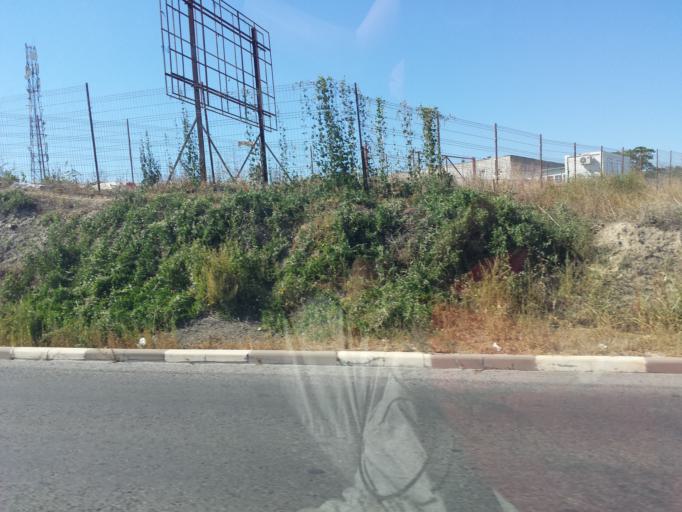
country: RO
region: Tulcea
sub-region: Municipiul Tulcea
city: Tulcea
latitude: 45.1625
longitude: 28.7890
